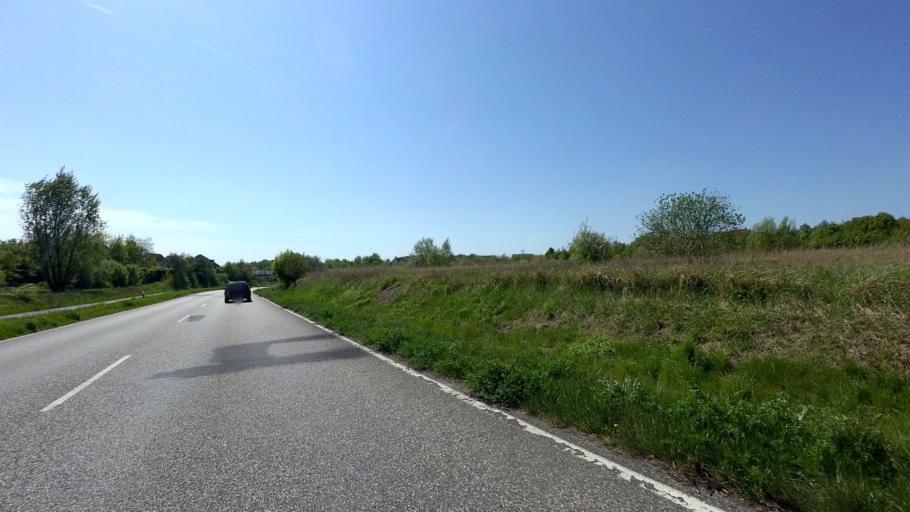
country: DE
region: Brandenburg
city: Konigs Wusterhausen
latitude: 52.3007
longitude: 13.6023
